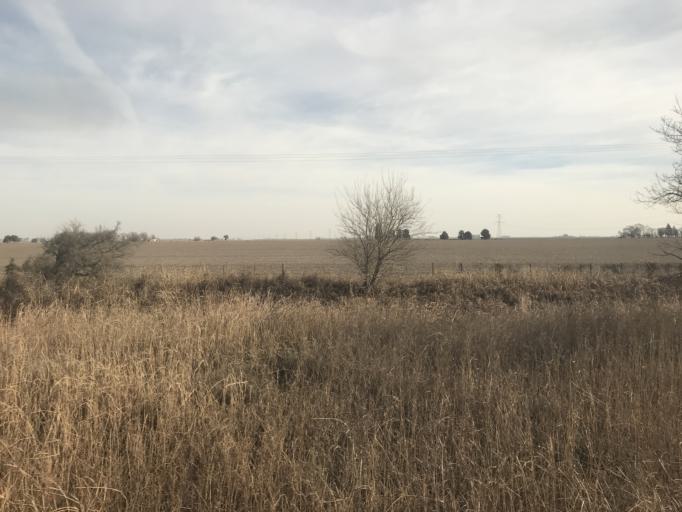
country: AR
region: Cordoba
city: Pilar
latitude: -31.7133
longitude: -63.8586
